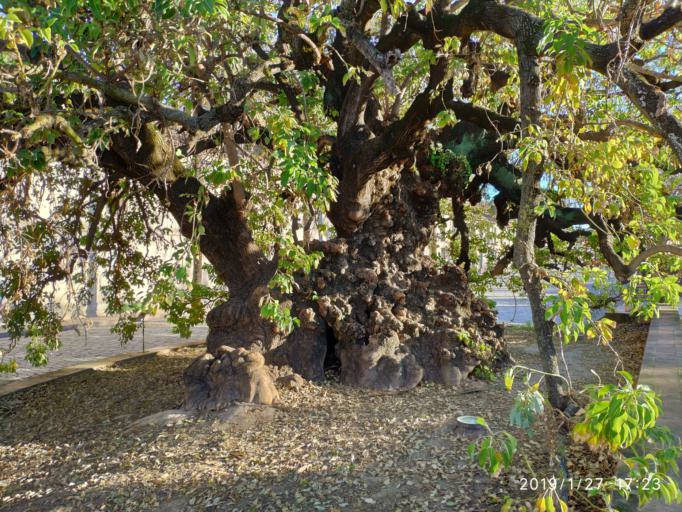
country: ES
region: Andalusia
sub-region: Provincia de Sevilla
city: Camas
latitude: 37.3981
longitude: -6.0081
